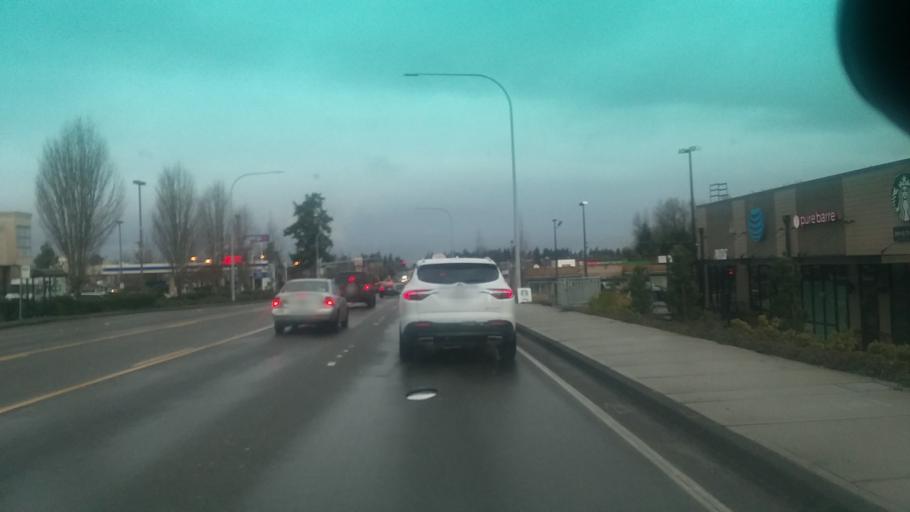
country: US
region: Washington
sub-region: Pierce County
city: South Hill
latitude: 47.1497
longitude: -122.2929
